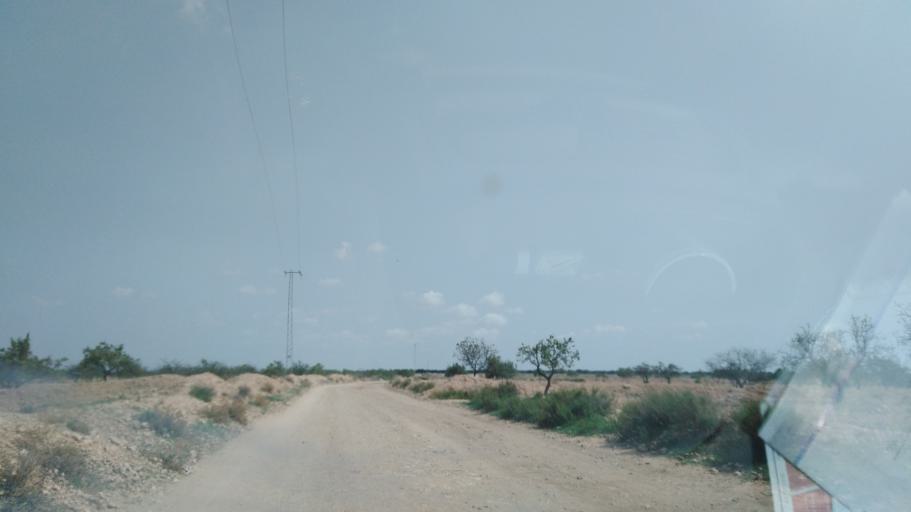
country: TN
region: Safaqis
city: Sfax
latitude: 34.6418
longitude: 10.6180
